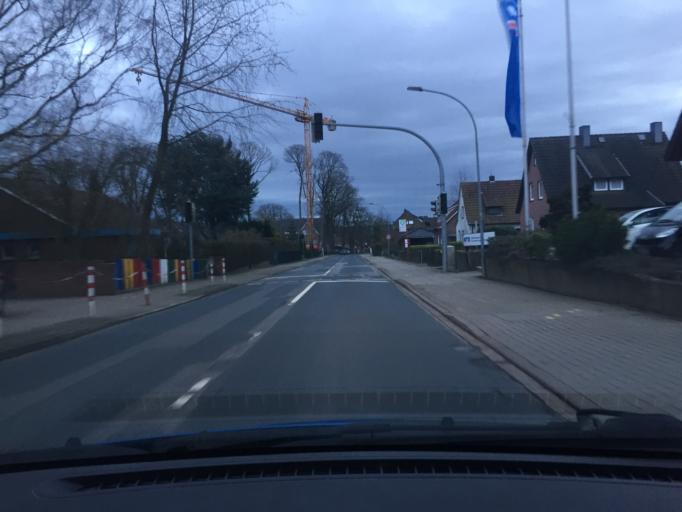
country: DE
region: Lower Saxony
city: Seevetal
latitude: 53.4356
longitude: 9.9060
